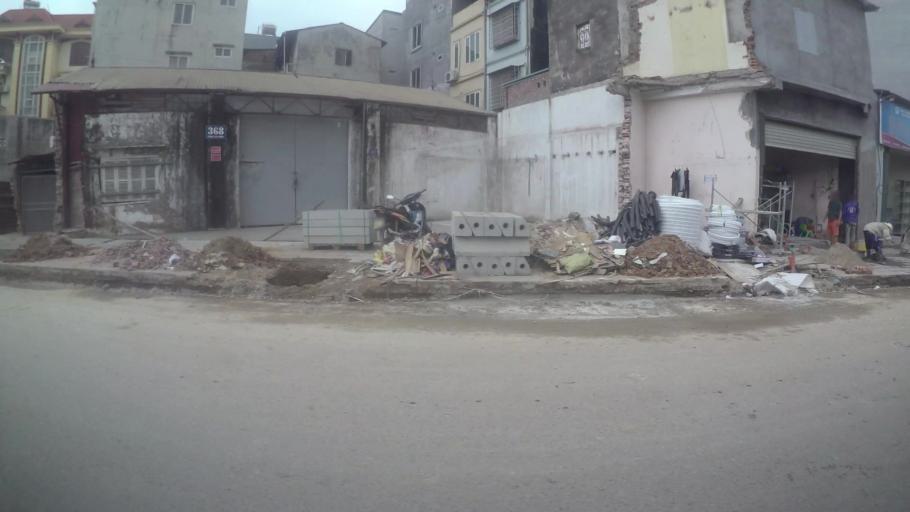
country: VN
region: Ha Noi
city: Cau Dien
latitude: 21.0581
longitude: 105.7826
